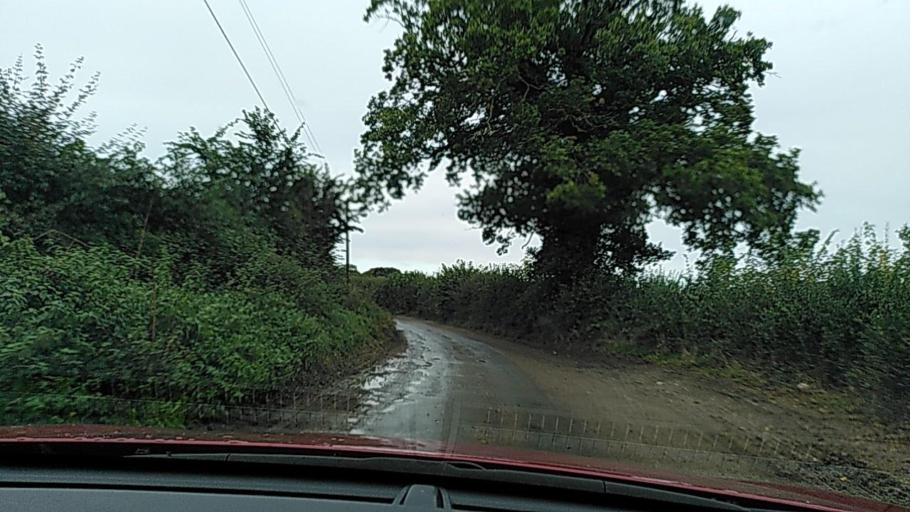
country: GB
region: England
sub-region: West Berkshire
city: Tilehurst
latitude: 51.4919
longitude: -1.0208
